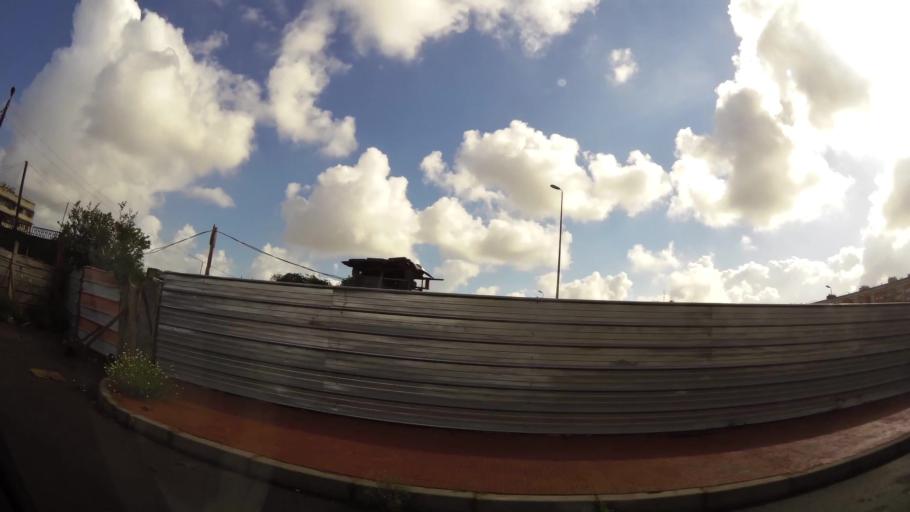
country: MA
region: Grand Casablanca
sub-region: Mediouna
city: Tit Mellil
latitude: 33.5786
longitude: -7.5292
